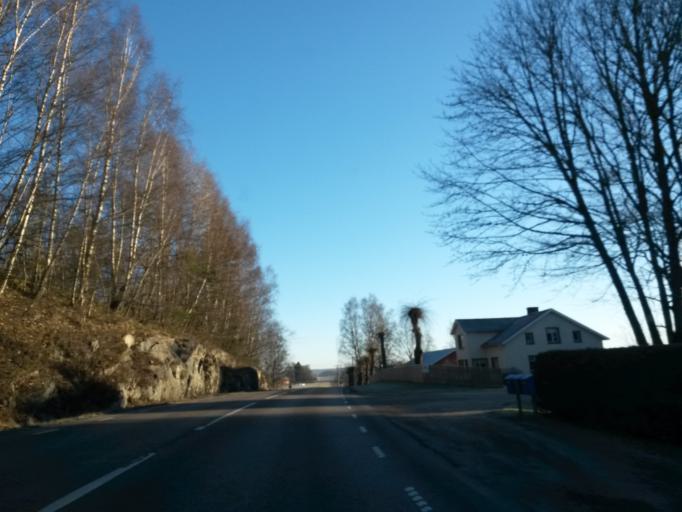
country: SE
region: Vaestra Goetaland
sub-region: Vargarda Kommun
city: Vargarda
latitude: 58.0553
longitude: 12.8994
